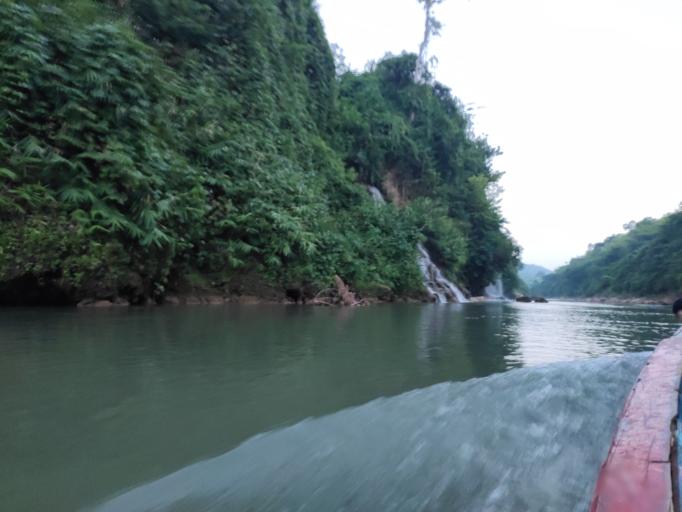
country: MM
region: Mandalay
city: Meiktila
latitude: 21.0140
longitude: 96.3931
